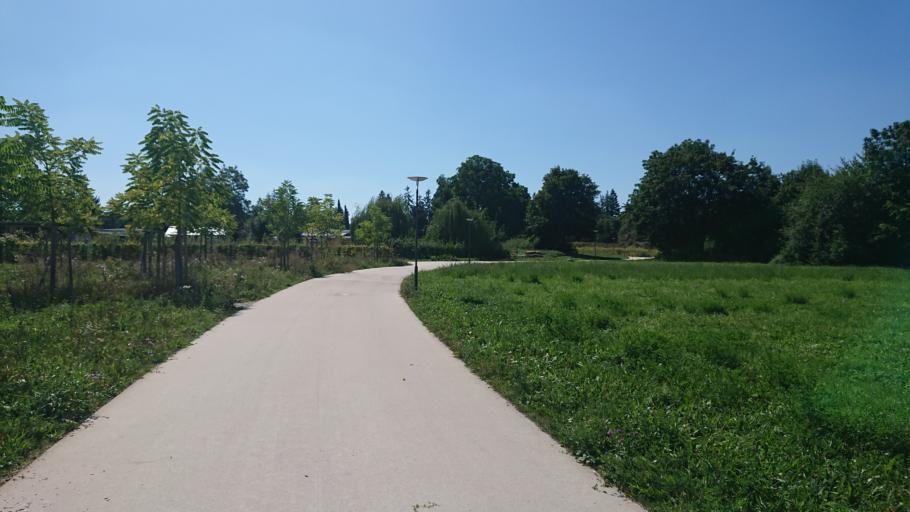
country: DE
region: Bavaria
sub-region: Swabia
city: Stadtbergen
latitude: 48.3697
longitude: 10.8639
